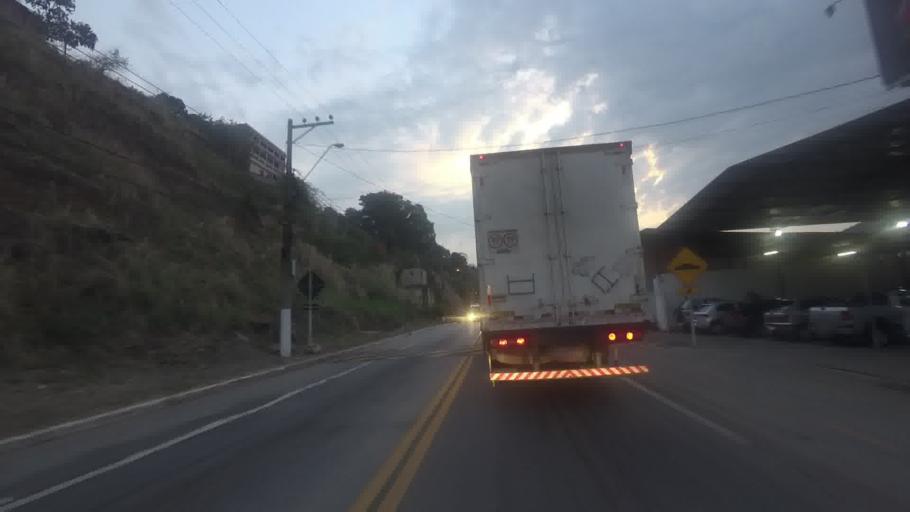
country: BR
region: Minas Gerais
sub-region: Alem Paraiba
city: Alem Paraiba
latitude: -21.8884
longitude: -42.7002
